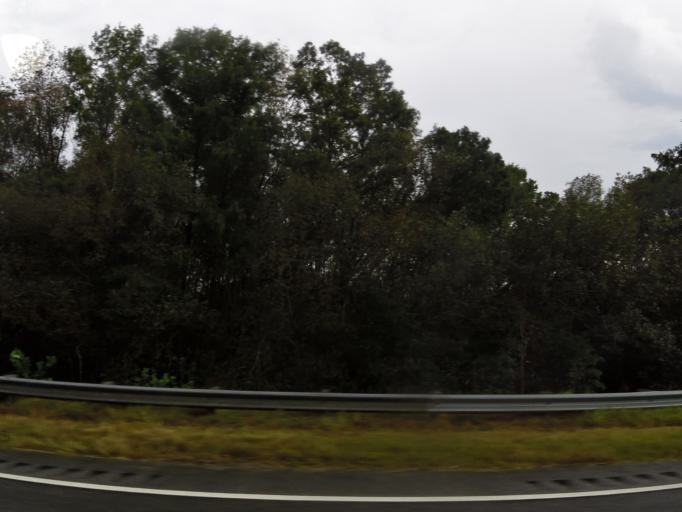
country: US
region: Georgia
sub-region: Long County
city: Ludowici
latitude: 31.7063
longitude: -81.7586
